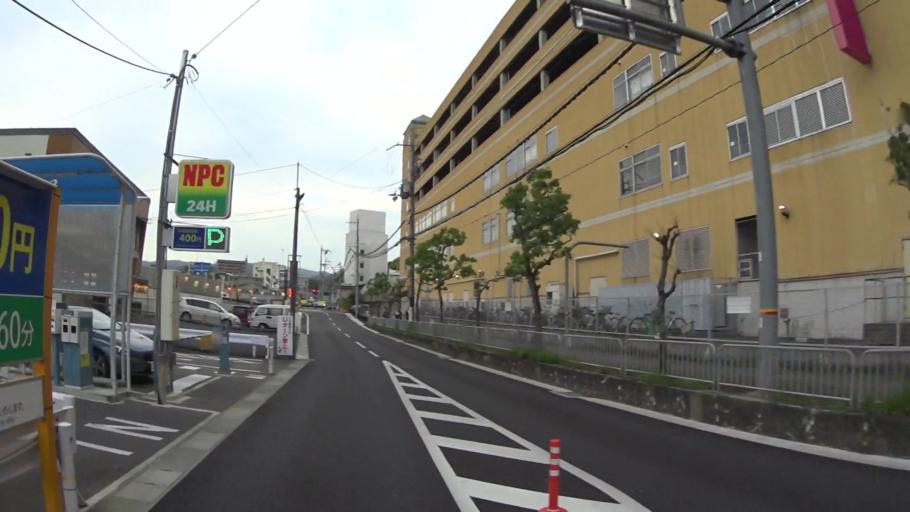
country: JP
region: Kyoto
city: Kameoka
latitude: 35.0153
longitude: 135.5846
